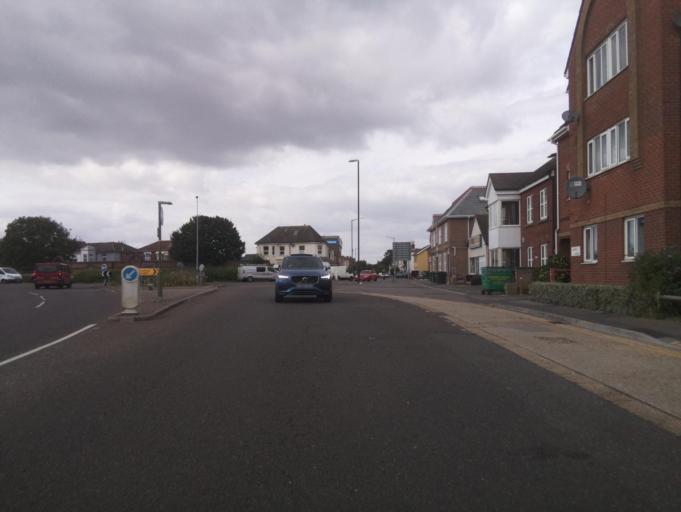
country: GB
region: England
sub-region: Bournemouth
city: Bournemouth
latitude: 50.7282
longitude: -1.8378
